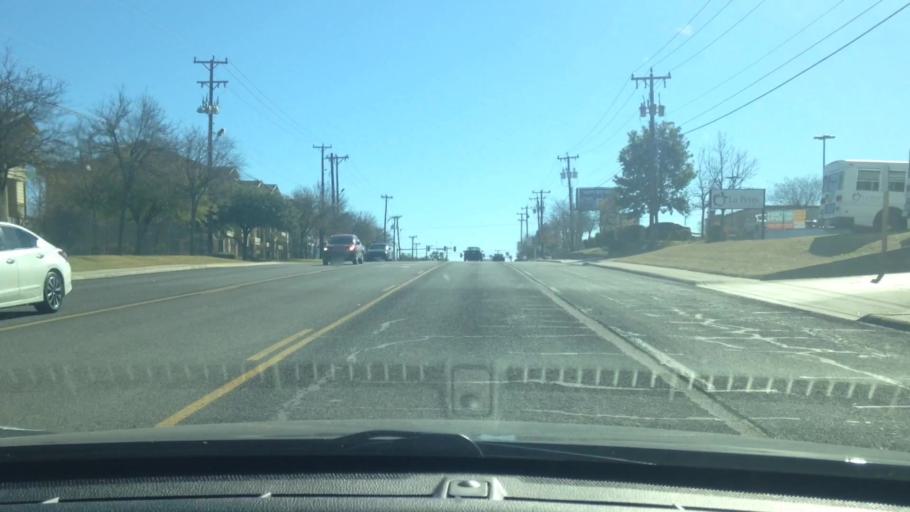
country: US
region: Texas
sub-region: Bexar County
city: Live Oak
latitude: 29.5892
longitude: -98.3790
